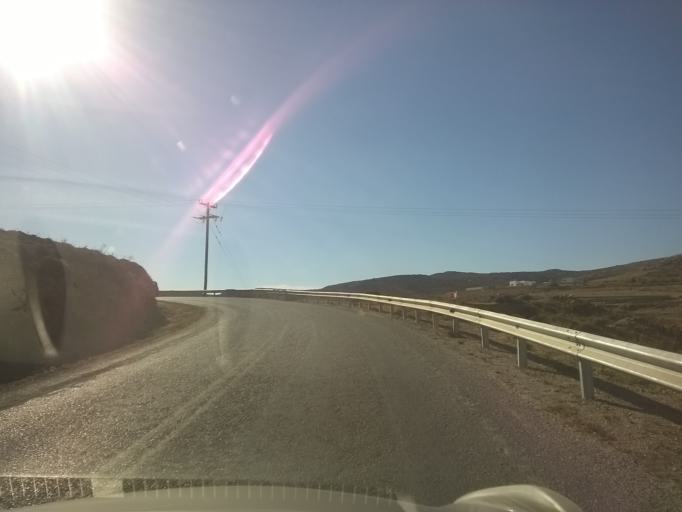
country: GR
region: South Aegean
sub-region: Nomos Kykladon
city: Naxos
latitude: 37.1199
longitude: 25.4148
